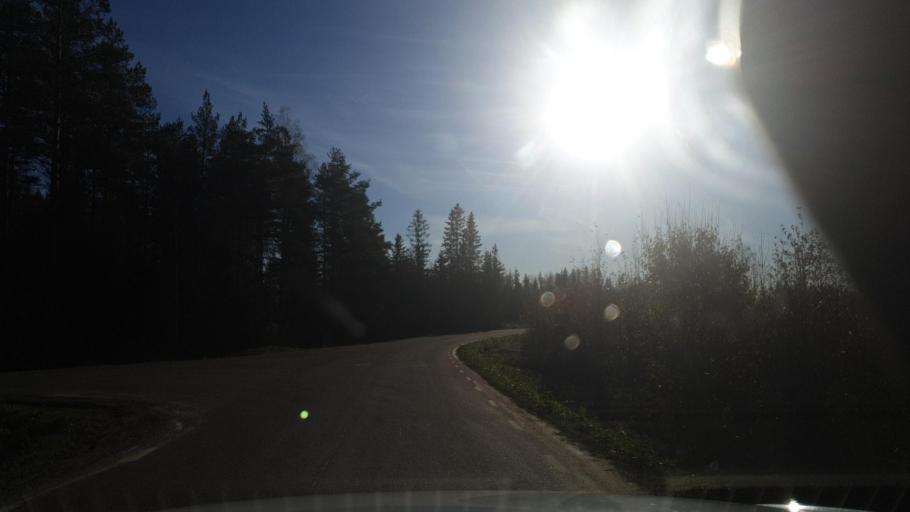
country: SE
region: Vaermland
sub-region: Karlstads Kommun
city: Edsvalla
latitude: 59.4783
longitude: 13.0776
